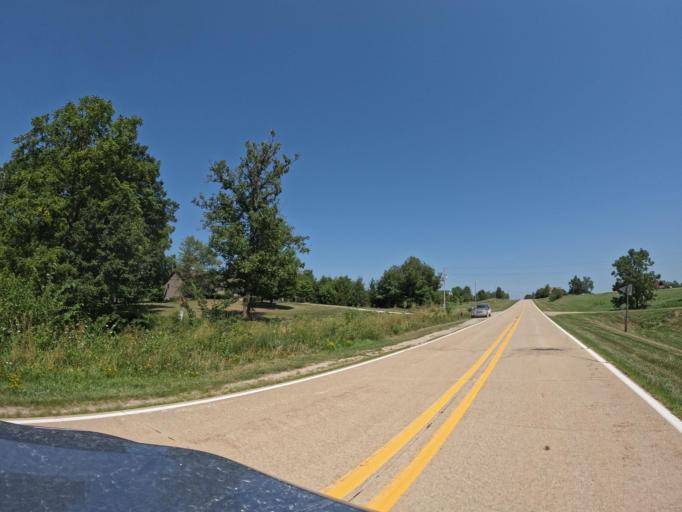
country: US
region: Iowa
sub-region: Henry County
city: Mount Pleasant
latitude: 40.8823
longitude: -91.5603
